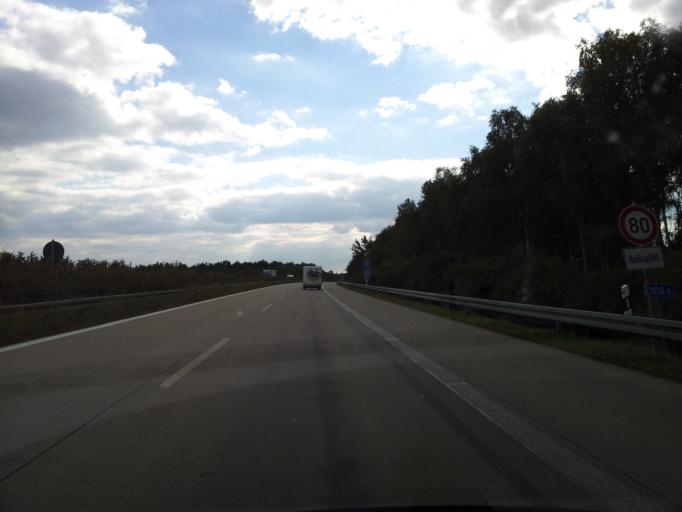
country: DE
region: Brandenburg
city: Schipkau
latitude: 51.5402
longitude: 13.9098
